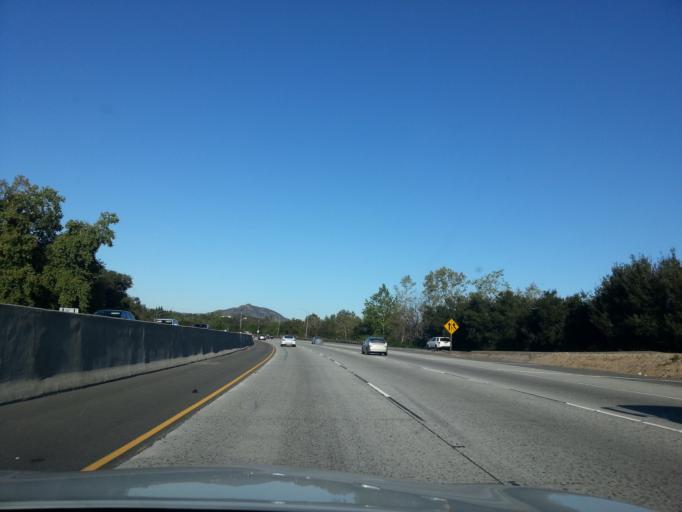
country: US
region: California
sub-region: Ventura County
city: Casa Conejo
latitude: 34.1839
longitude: -118.8922
